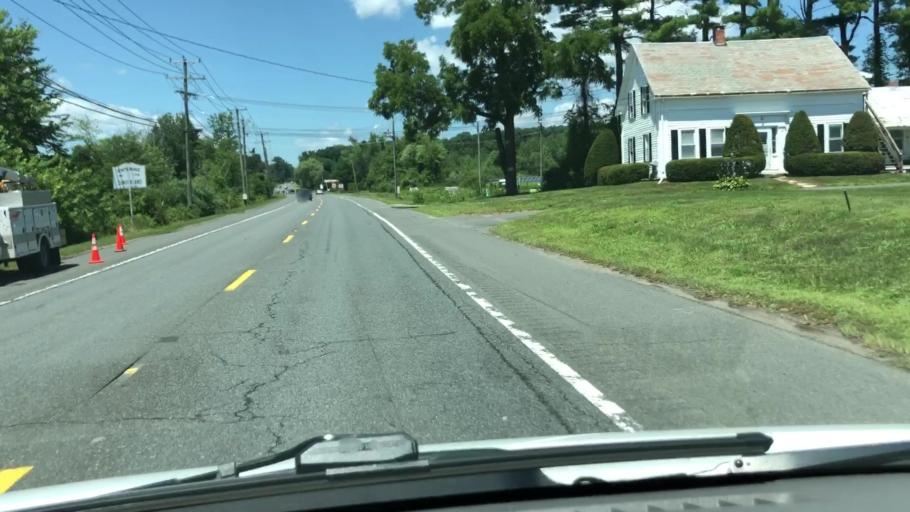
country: US
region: Massachusetts
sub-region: Hampshire County
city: North Amherst
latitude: 42.4274
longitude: -72.5403
